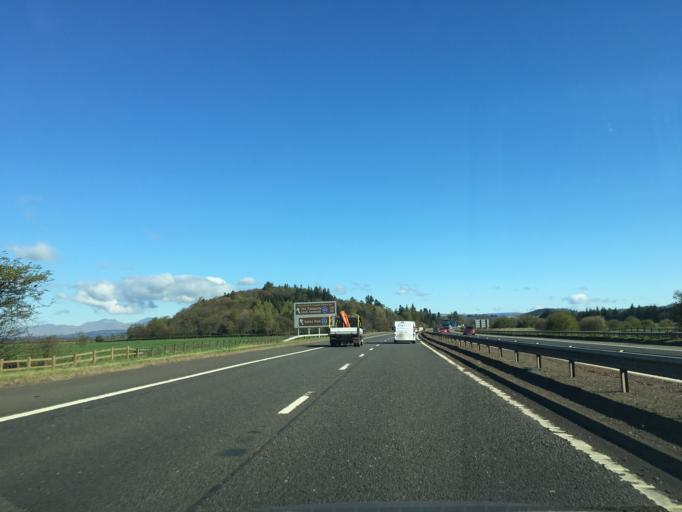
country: GB
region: Scotland
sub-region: Stirling
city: Stirling
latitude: 56.1219
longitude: -3.9703
